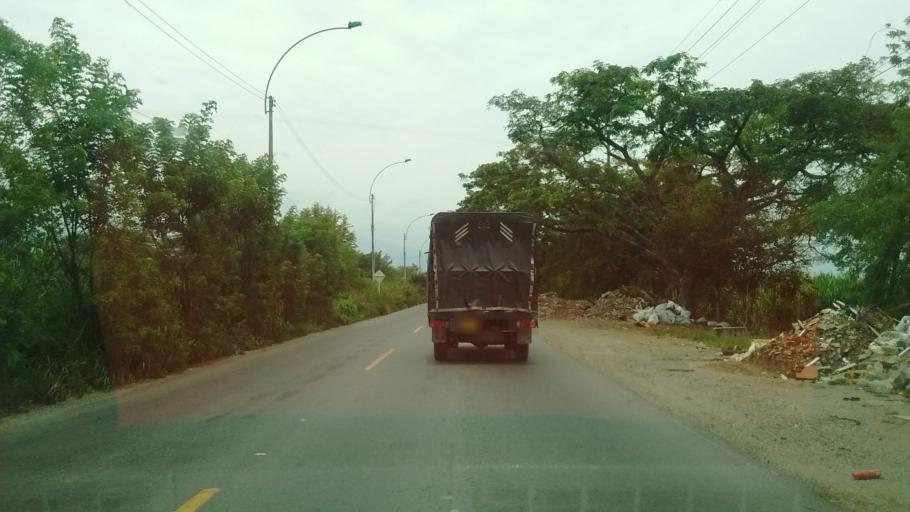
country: CO
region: Valle del Cauca
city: Jamundi
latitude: 3.3265
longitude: -76.5033
